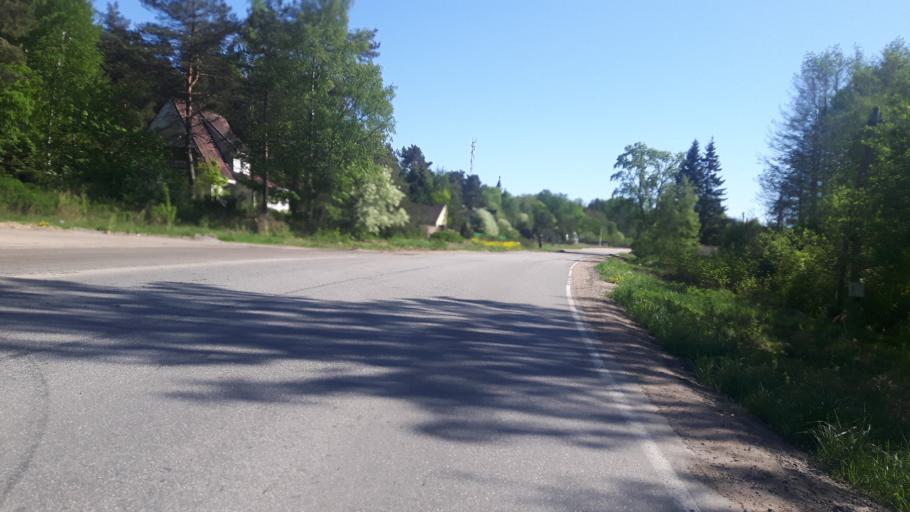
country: RU
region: Leningrad
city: Sosnovyy Bor
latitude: 60.2215
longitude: 29.0094
